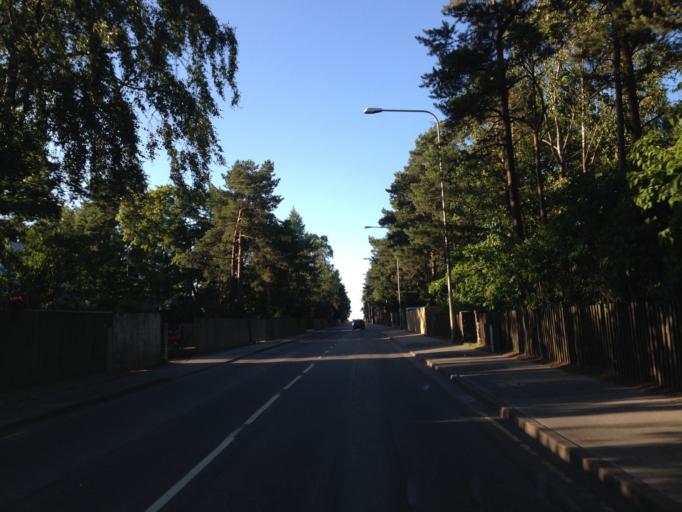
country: EE
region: Harju
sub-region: Saue vald
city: Laagri
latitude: 59.3798
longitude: 24.6369
